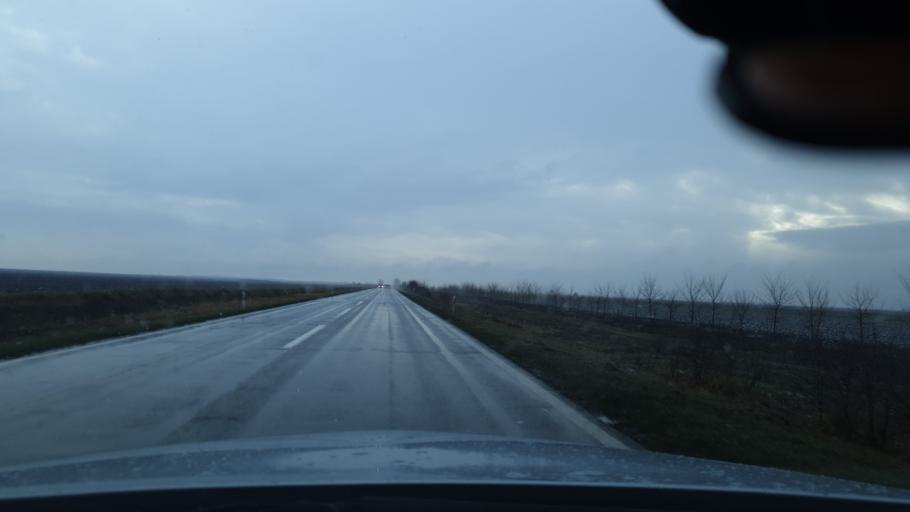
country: RS
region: Autonomna Pokrajina Vojvodina
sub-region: Juznobanatski Okrug
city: Pancevo
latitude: 44.8438
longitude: 20.7906
